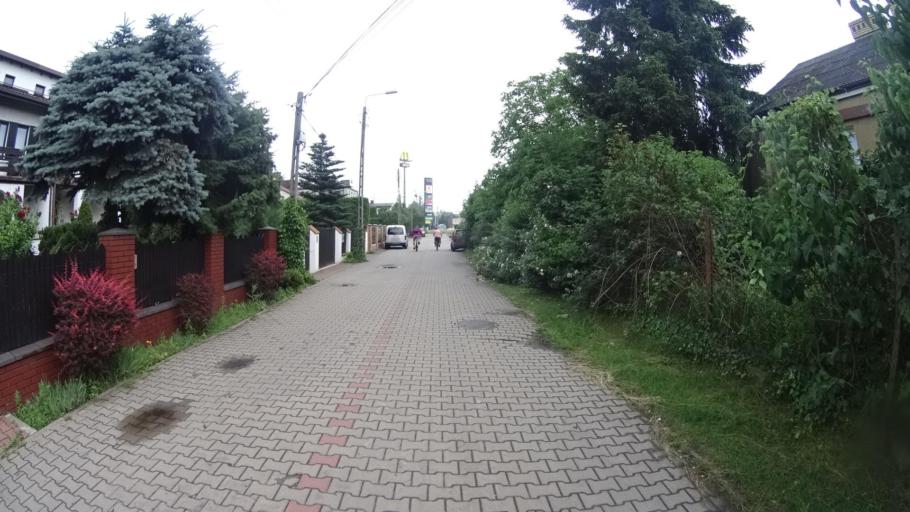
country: PL
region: Masovian Voivodeship
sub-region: Powiat pruszkowski
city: Piastow
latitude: 52.1913
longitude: 20.8524
